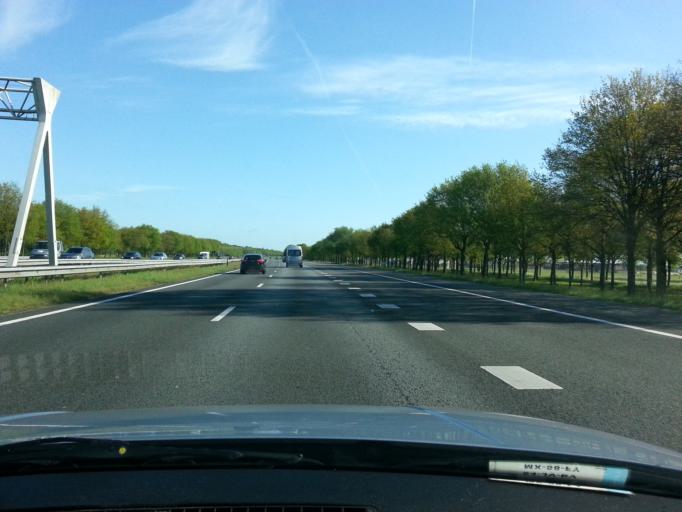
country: NL
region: North Holland
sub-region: Gemeente Laren
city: Laren
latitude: 52.2398
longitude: 5.2456
